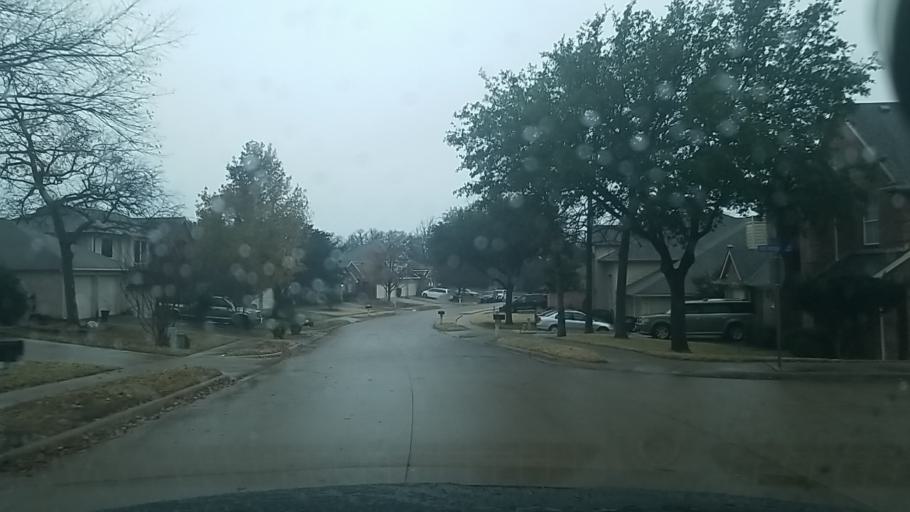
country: US
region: Texas
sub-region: Denton County
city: Corinth
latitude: 33.1578
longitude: -97.0759
